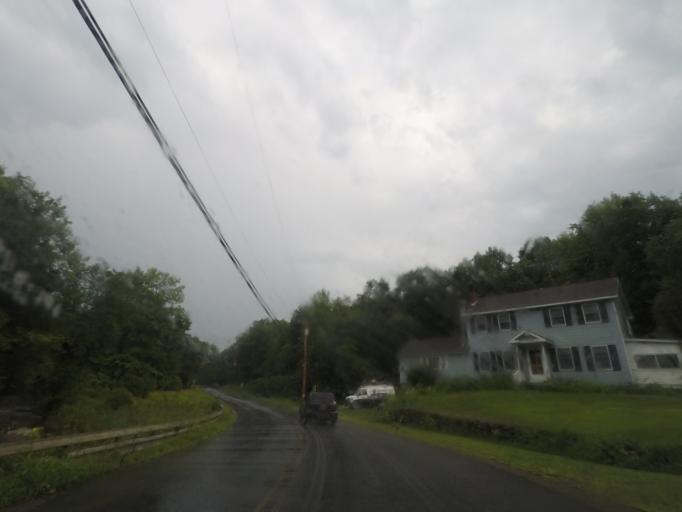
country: US
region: New York
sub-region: Rensselaer County
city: Poestenkill
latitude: 42.6783
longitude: -73.5395
